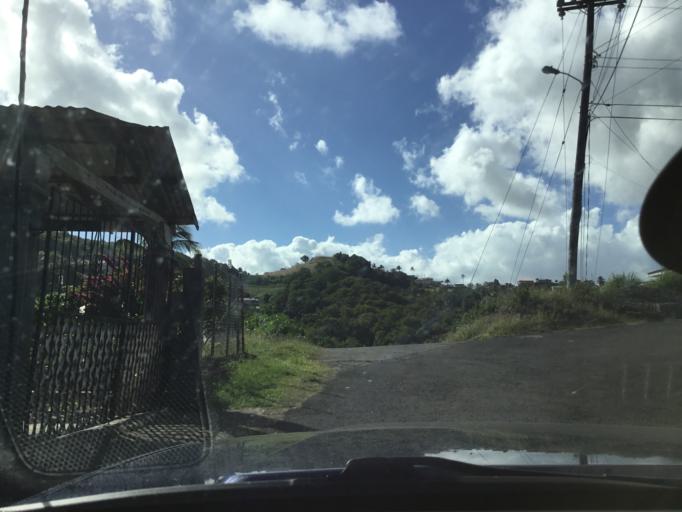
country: VC
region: Saint George
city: Kingstown
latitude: 13.1471
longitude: -61.1789
